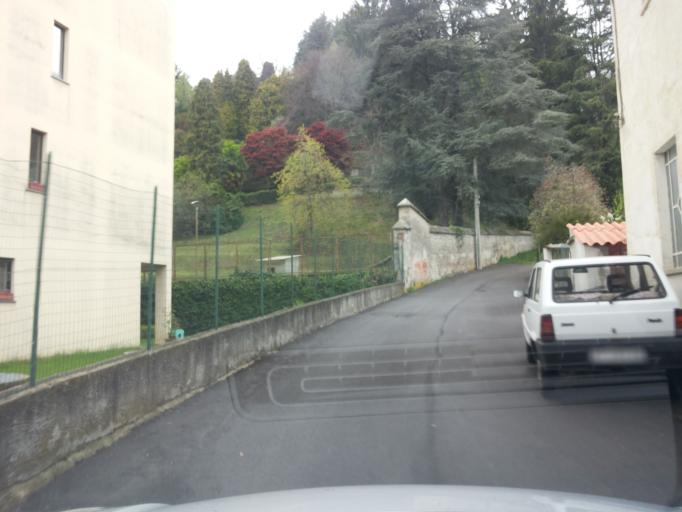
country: IT
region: Piedmont
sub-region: Provincia di Biella
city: Biella
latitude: 45.5744
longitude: 8.0653
